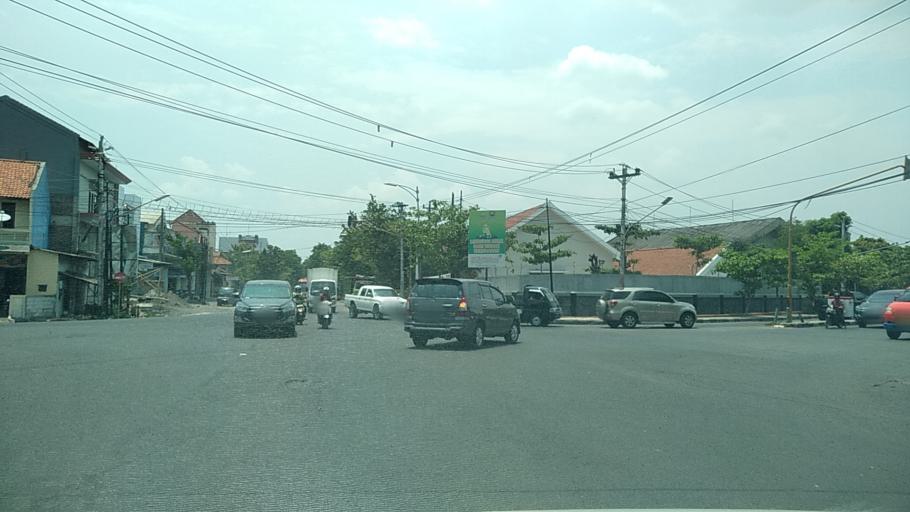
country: ID
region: Central Java
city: Semarang
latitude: -6.9640
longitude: 110.4309
